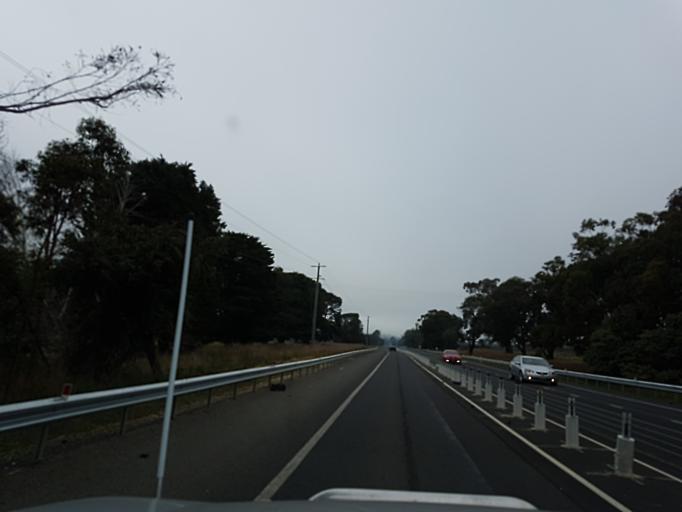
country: AU
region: Victoria
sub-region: Murrindindi
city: Alexandra
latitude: -37.2083
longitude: 145.4566
